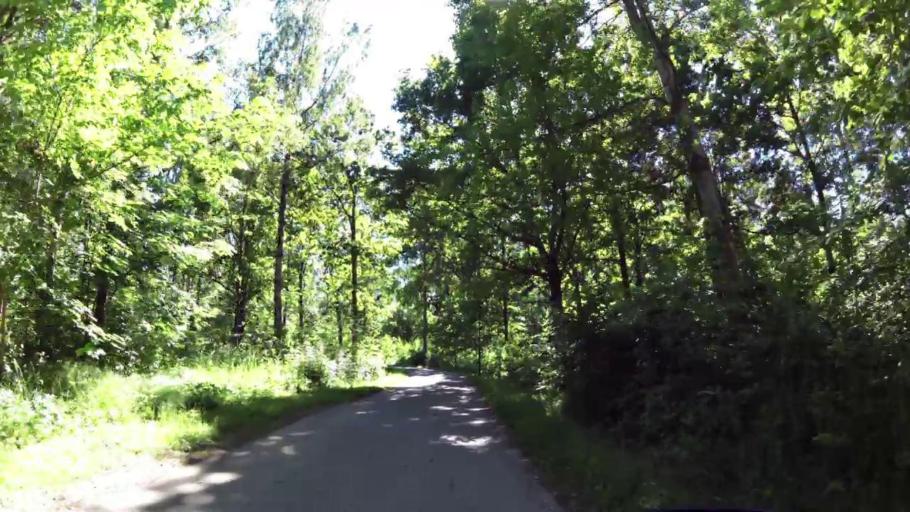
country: SE
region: OEstergoetland
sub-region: Linkopings Kommun
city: Linkoping
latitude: 58.3965
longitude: 15.6105
